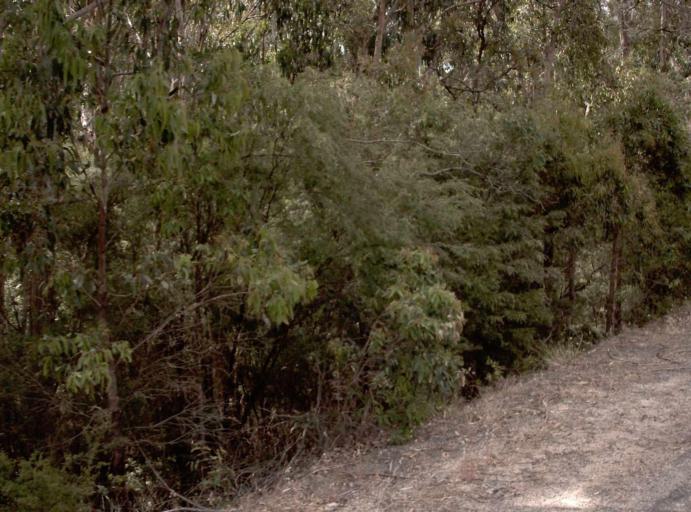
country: AU
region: New South Wales
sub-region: Bega Valley
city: Eden
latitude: -37.4623
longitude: 149.5883
